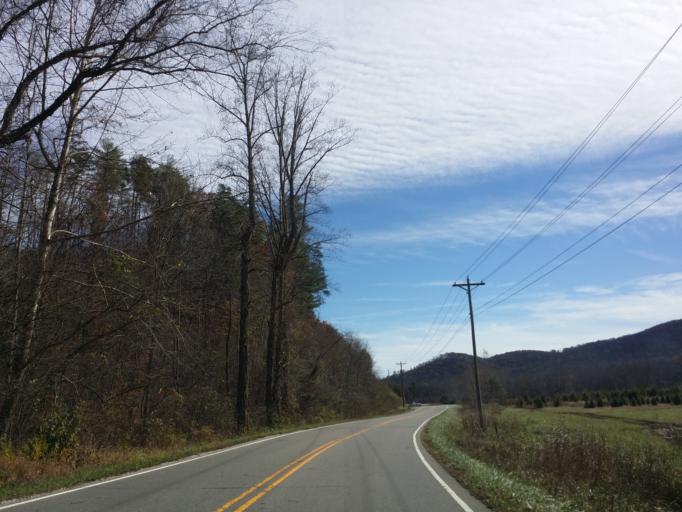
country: US
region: North Carolina
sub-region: Mitchell County
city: Spruce Pine
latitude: 35.8012
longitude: -82.0373
